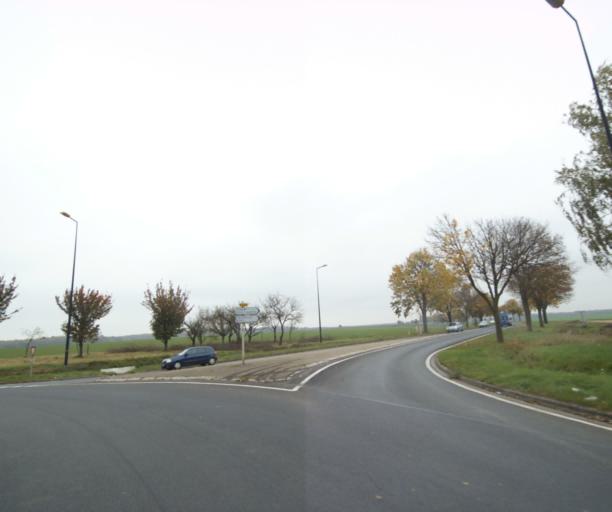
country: FR
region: Lorraine
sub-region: Departement de Meurthe-et-Moselle
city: Briey
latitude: 49.2555
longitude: 5.9486
